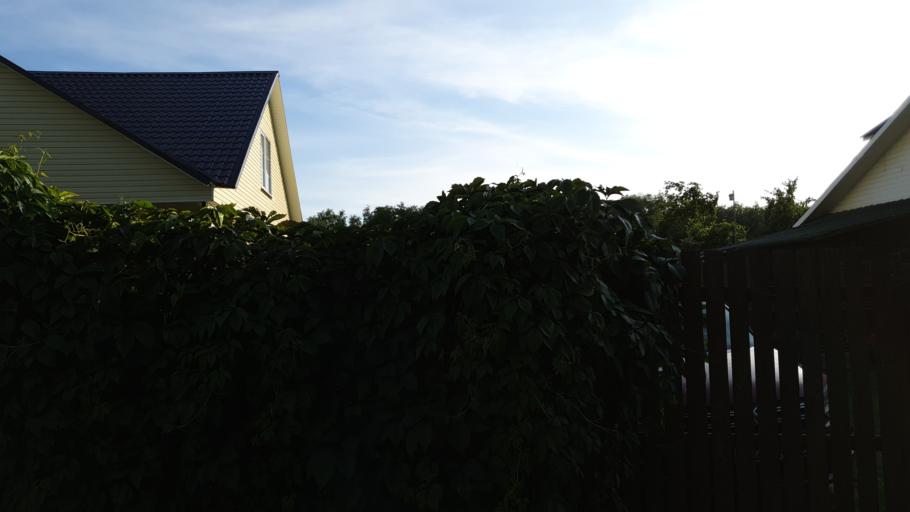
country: RU
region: Leningrad
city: Ivangorod
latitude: 59.4232
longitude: 28.3344
